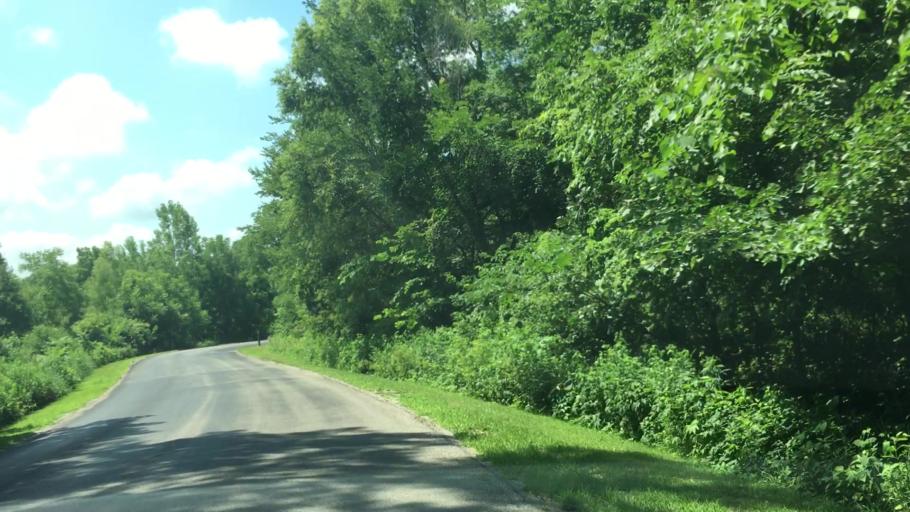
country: US
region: Iowa
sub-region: Johnson County
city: Tiffin
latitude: 41.7208
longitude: -91.7245
